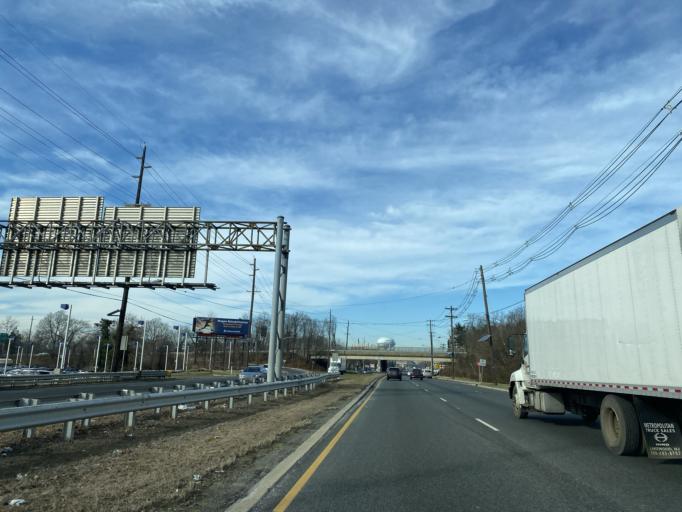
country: US
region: New Jersey
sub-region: Burlington County
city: Maple Shade
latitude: 39.9446
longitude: -74.9804
